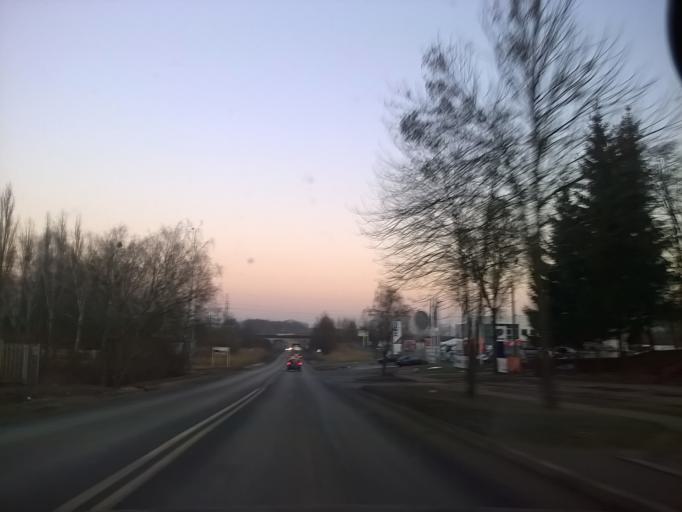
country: PL
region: Warmian-Masurian Voivodeship
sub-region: Powiat olsztynski
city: Olsztyn
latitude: 53.7824
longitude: 20.5441
